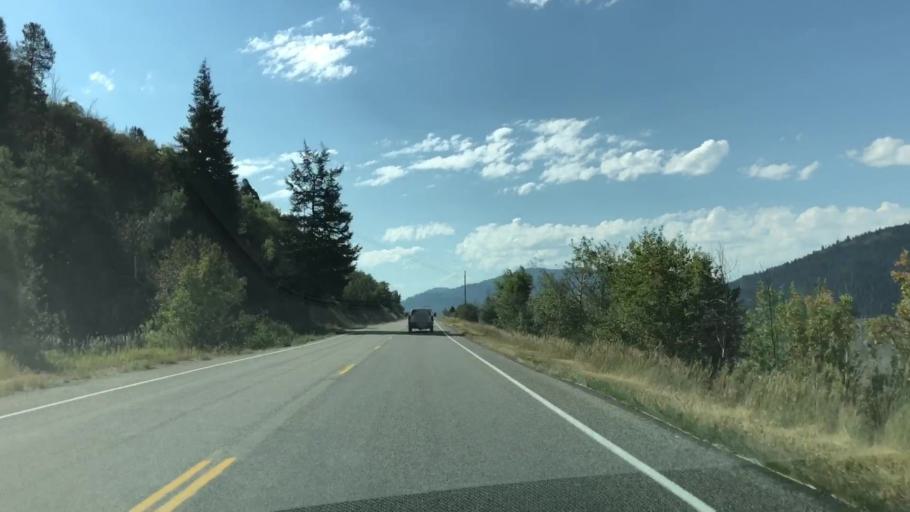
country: US
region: Idaho
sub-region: Teton County
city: Victor
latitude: 43.3387
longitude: -111.2003
